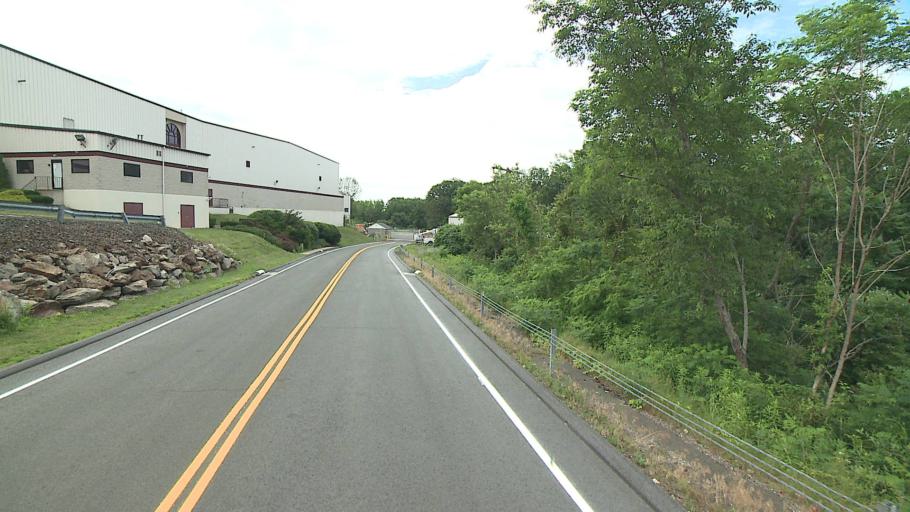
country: US
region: Connecticut
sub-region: New Haven County
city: Oxford
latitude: 41.4780
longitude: -73.1388
